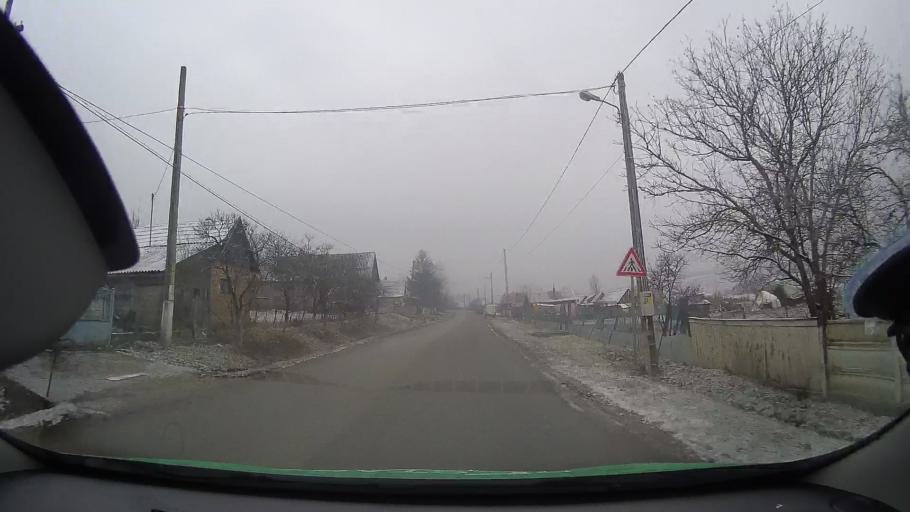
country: RO
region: Alba
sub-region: Comuna Noslac
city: Noslac
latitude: 46.3477
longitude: 23.9391
